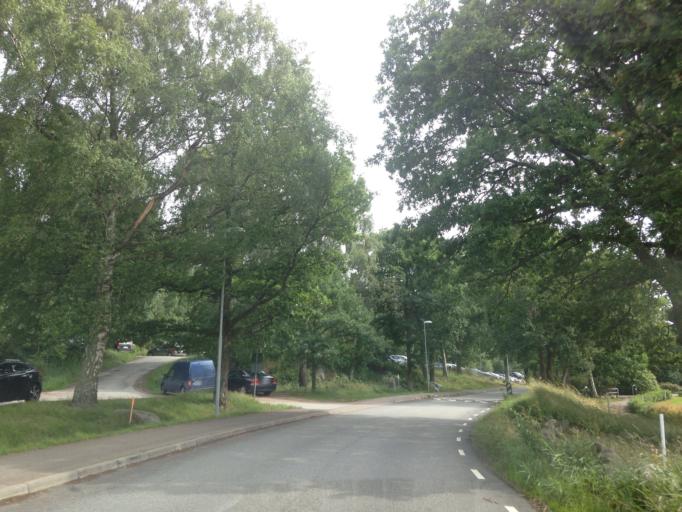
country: SE
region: Vaestra Goetaland
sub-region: Goteborg
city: Goeteborg
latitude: 57.7791
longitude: 11.9561
